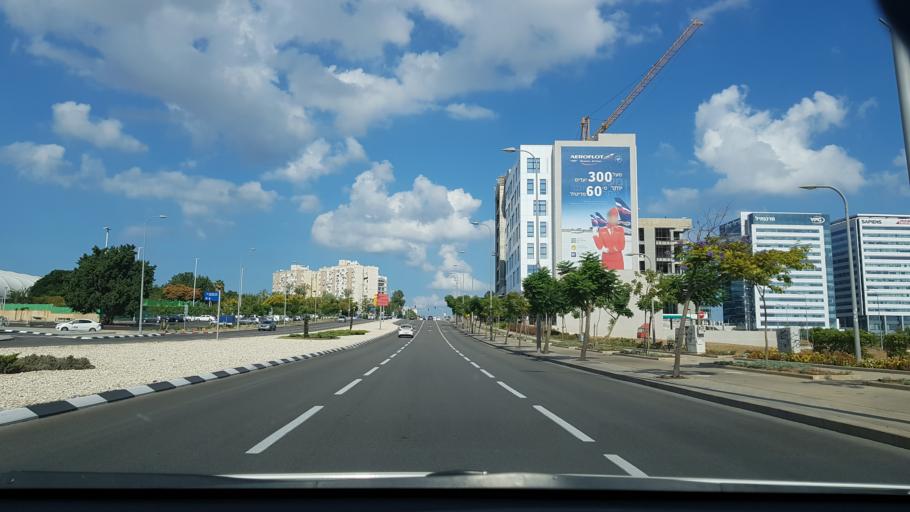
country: IL
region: Tel Aviv
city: Azor
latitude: 32.0035
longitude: 34.8016
